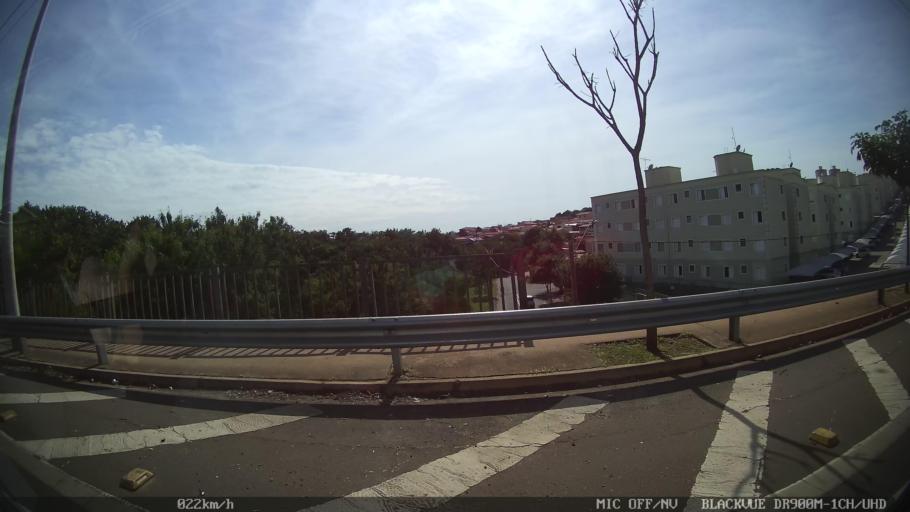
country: BR
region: Sao Paulo
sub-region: Piracicaba
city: Piracicaba
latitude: -22.7466
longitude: -47.6264
